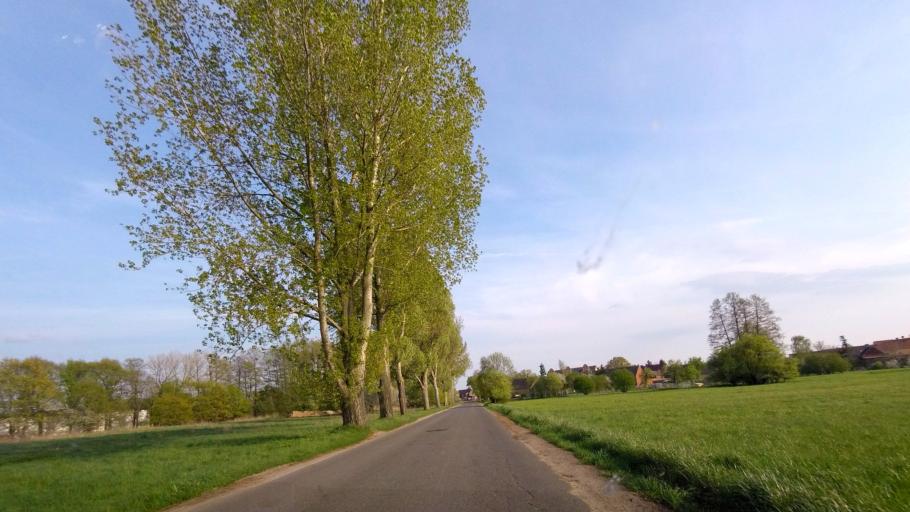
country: DE
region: Saxony-Anhalt
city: Zahna
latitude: 51.9153
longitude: 12.7943
